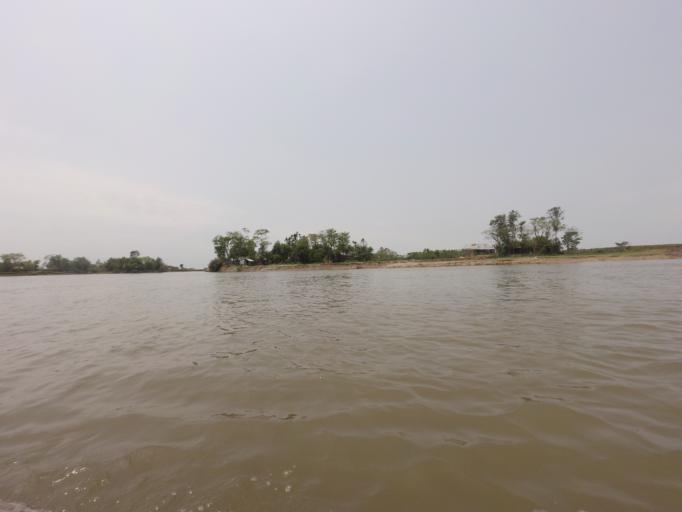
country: BD
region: Sylhet
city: Sylhet
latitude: 25.0084
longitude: 91.9157
